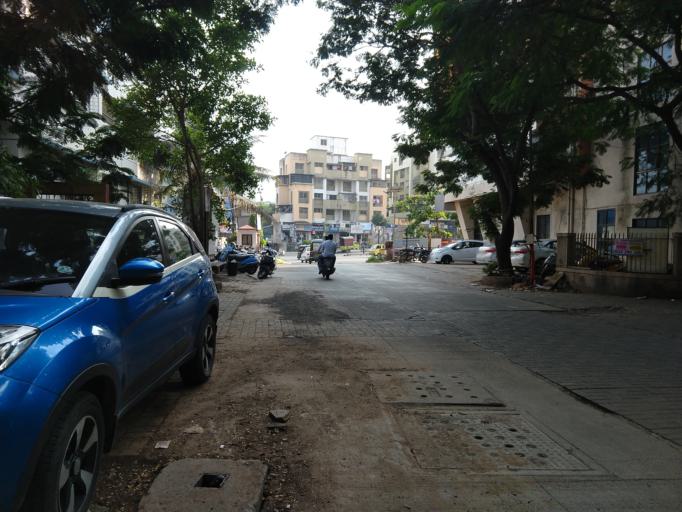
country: IN
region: Maharashtra
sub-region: Pune Division
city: Shivaji Nagar
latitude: 18.5089
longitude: 73.7904
